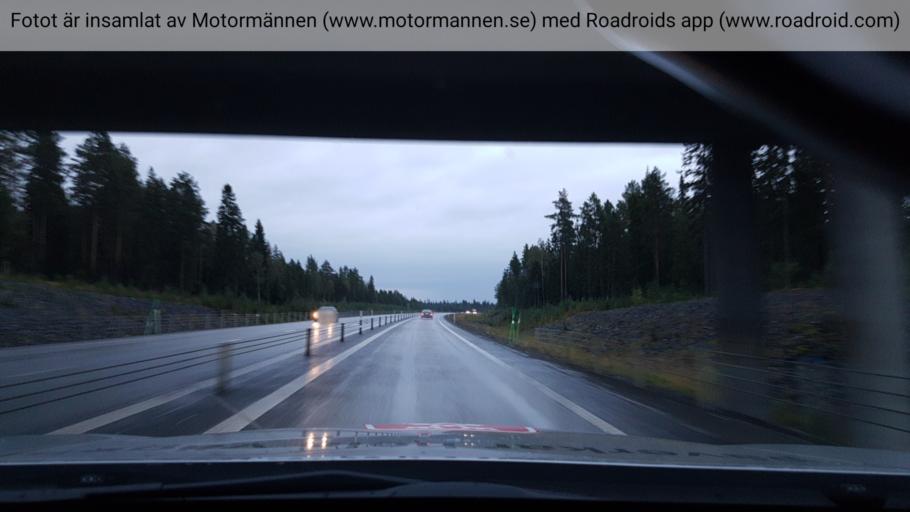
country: SE
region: Vaesterbotten
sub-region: Umea Kommun
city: Umea
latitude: 63.8562
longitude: 20.2344
